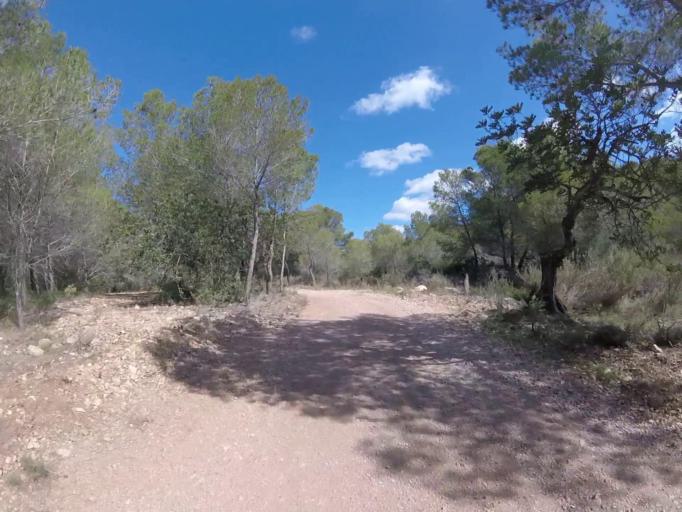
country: ES
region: Valencia
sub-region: Provincia de Castello
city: Alcoceber
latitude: 40.2924
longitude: 0.3146
